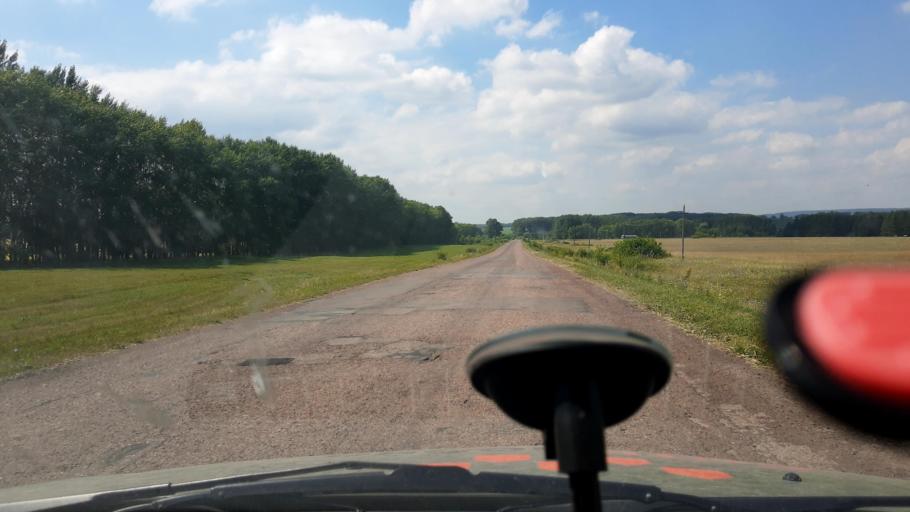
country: RU
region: Bashkortostan
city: Chekmagush
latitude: 54.8864
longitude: 54.5872
